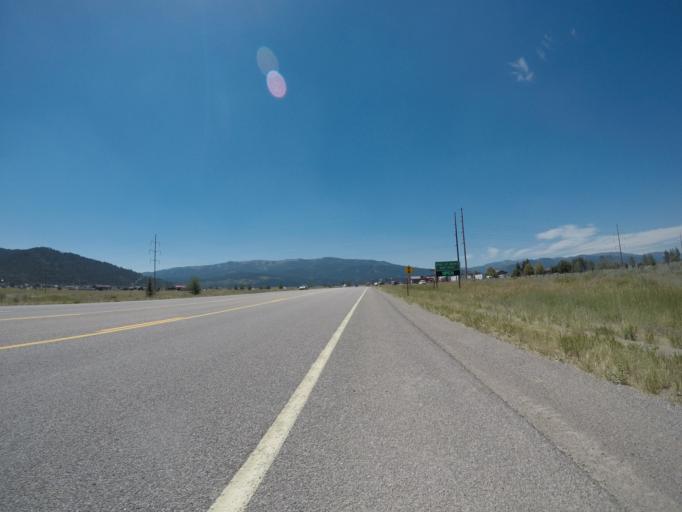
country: US
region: Wyoming
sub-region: Teton County
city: Hoback
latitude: 43.1732
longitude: -111.0140
